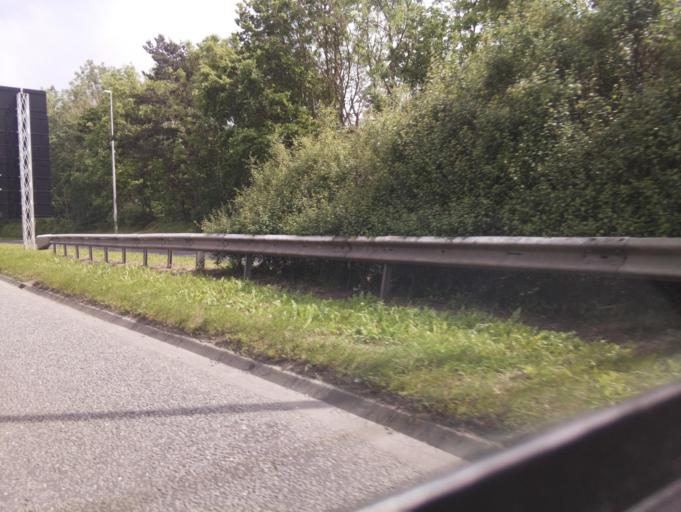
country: GB
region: England
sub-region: Sunderland
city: Washington
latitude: 54.9054
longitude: -1.5109
